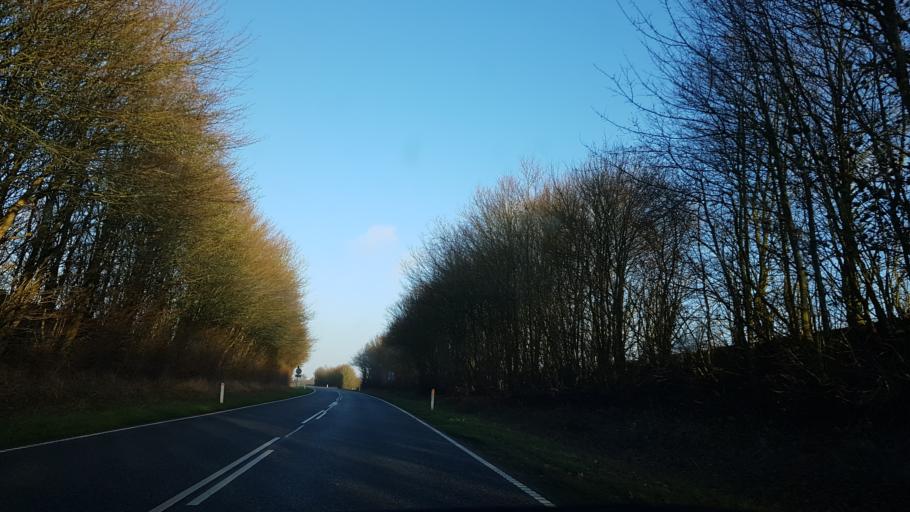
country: DK
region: South Denmark
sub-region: Haderslev Kommune
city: Haderslev
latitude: 55.2035
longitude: 9.4540
